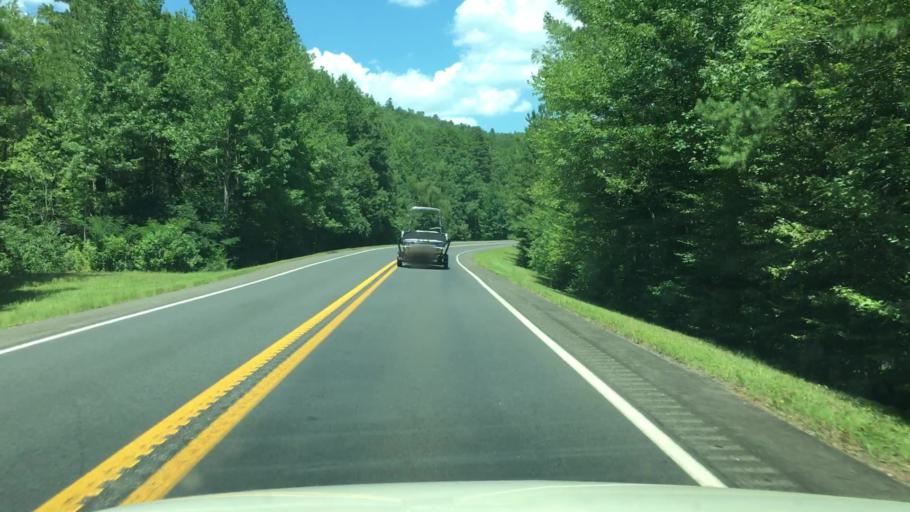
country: US
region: Arkansas
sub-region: Garland County
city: Lake Hamilton
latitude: 34.3584
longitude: -93.1779
